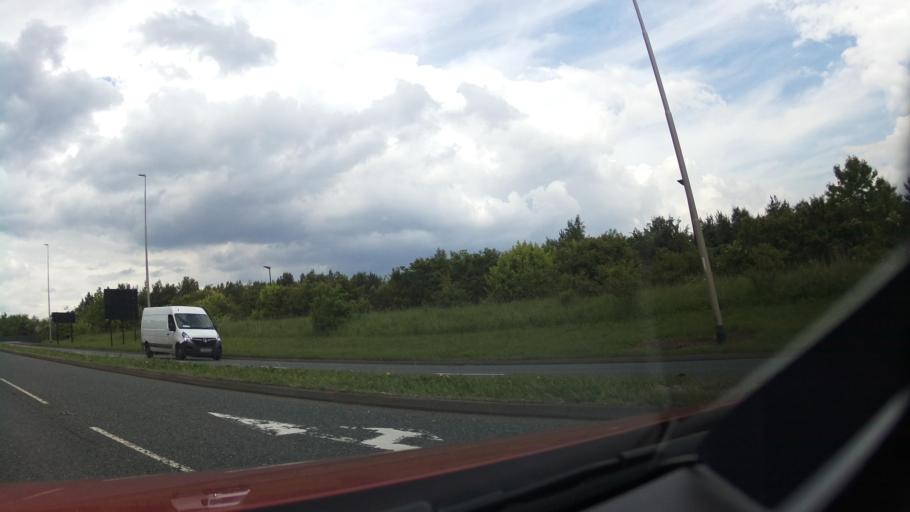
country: GB
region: England
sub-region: Sunderland
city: Washington
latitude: 54.9041
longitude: -1.5552
